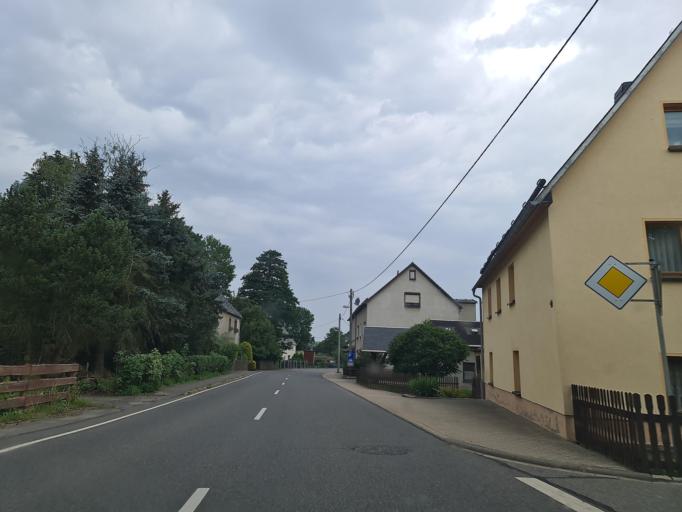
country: DE
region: Saxony
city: Eppendorf
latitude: 50.7866
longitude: 13.2663
